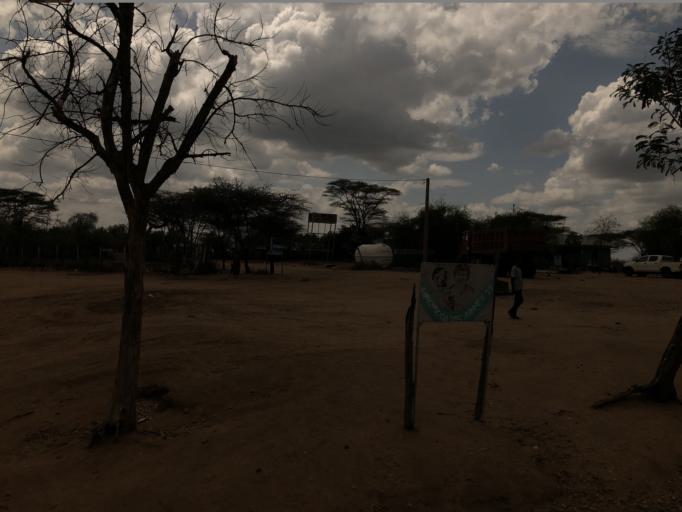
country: ET
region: Southern Nations, Nationalities, and People's Region
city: Turmi
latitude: 4.9680
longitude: 36.4886
